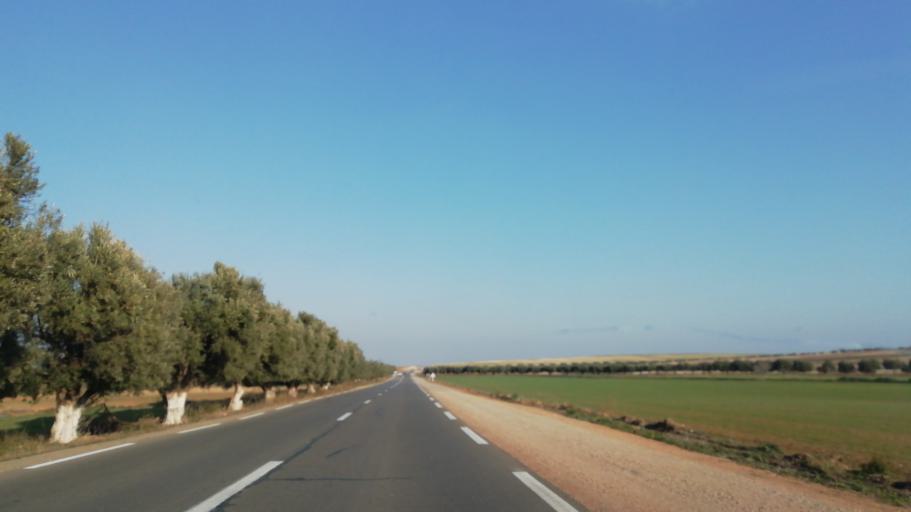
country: DZ
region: Sidi Bel Abbes
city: Sidi Bel Abbes
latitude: 35.1763
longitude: -0.8184
